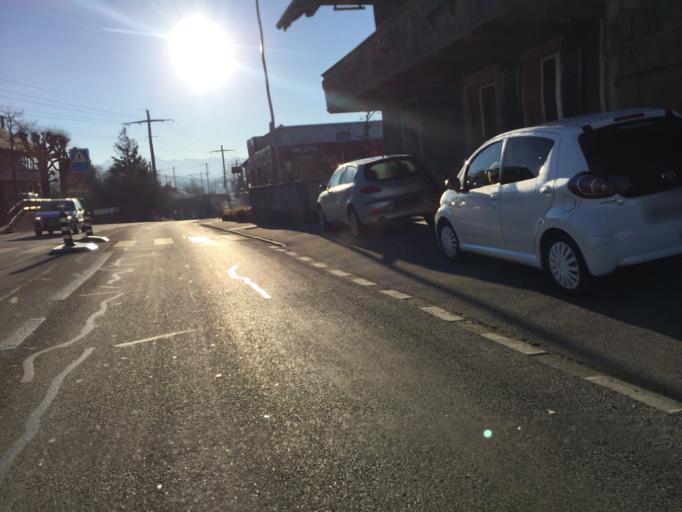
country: CH
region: Bern
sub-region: Bern-Mittelland District
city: Rubigen
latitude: 46.8936
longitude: 7.5480
